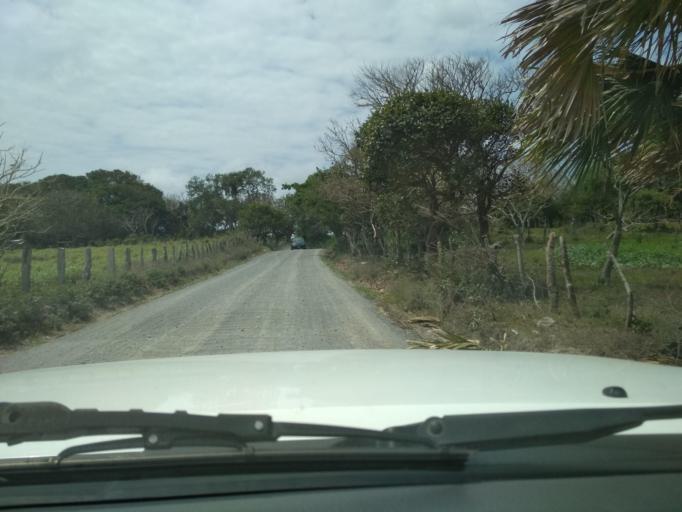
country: MX
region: Veracruz
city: Anton Lizardo
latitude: 19.0079
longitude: -95.9847
